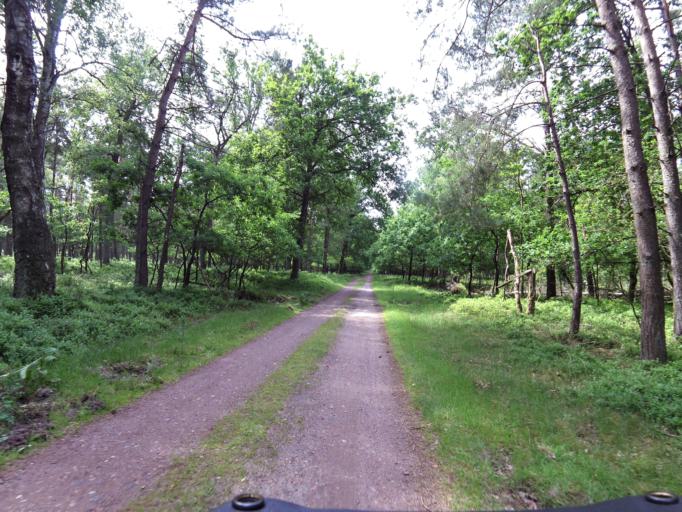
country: NL
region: Gelderland
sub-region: Gemeente Apeldoorn
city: Beekbergen
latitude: 52.0960
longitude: 5.9465
